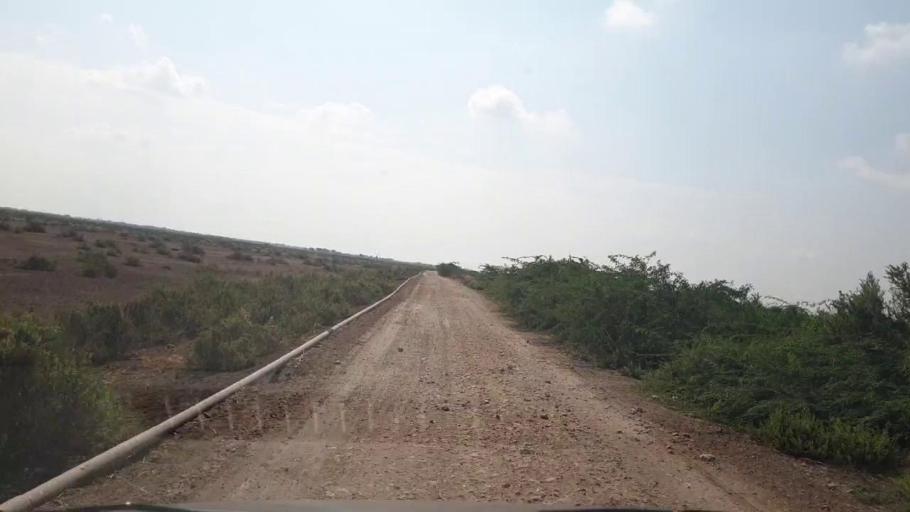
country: PK
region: Sindh
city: Badin
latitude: 24.5054
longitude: 68.6081
